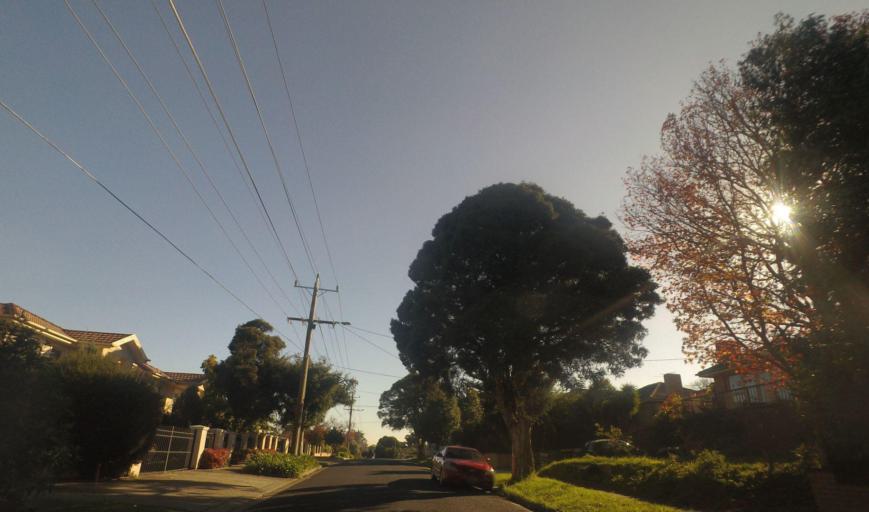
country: AU
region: Victoria
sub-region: Manningham
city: Doncaster
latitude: -37.7931
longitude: 145.1326
